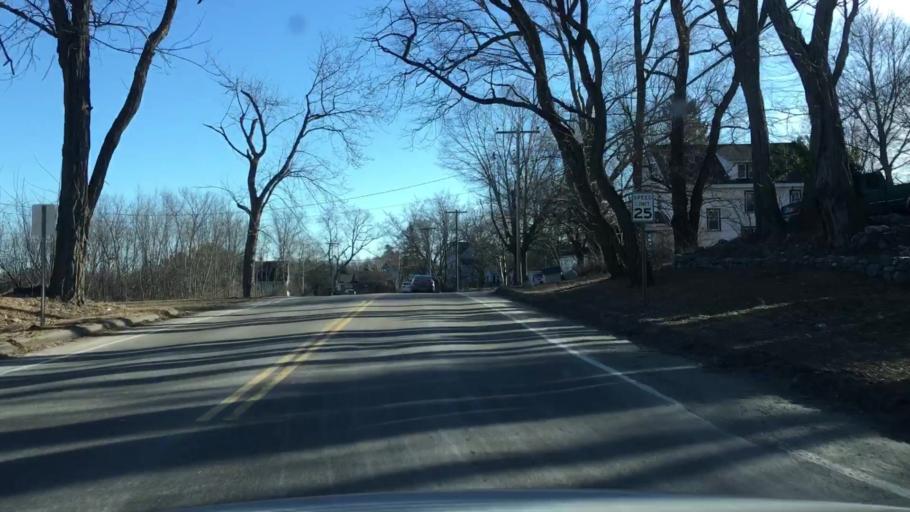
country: US
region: Maine
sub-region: Penobscot County
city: Bangor
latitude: 44.8138
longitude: -68.7962
